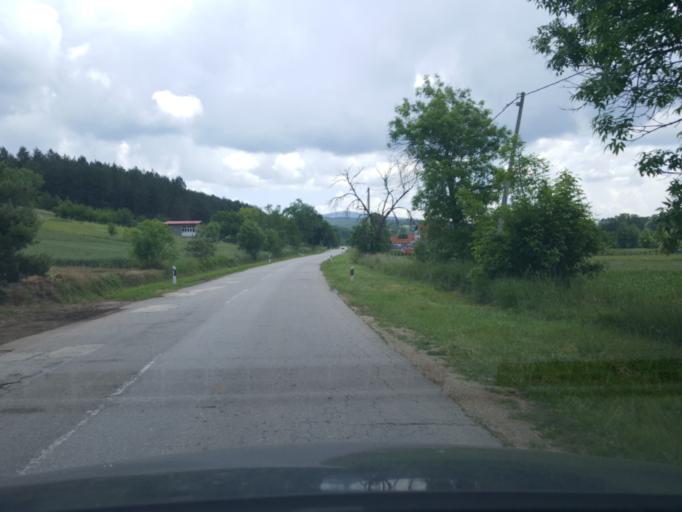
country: RS
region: Central Serbia
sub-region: Zajecarski Okrug
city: Soko Banja
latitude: 43.6464
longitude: 21.9103
